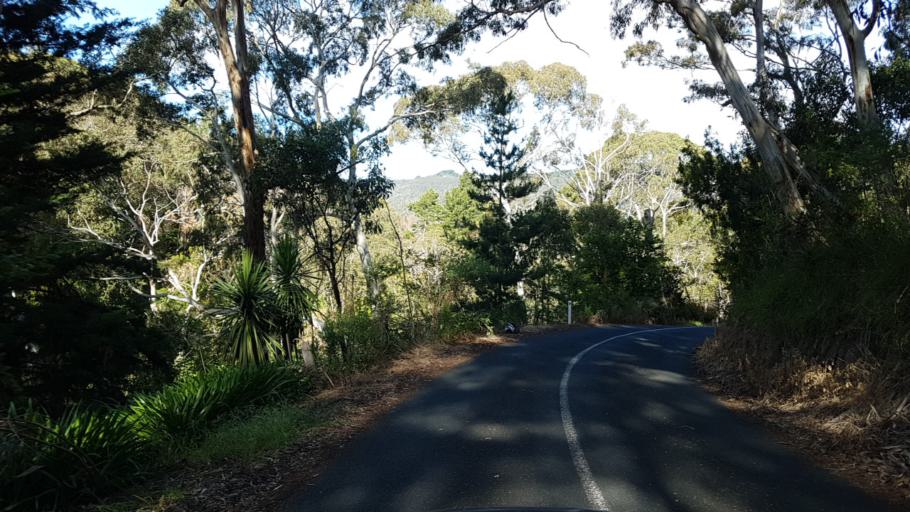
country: AU
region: South Australia
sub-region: Adelaide Hills
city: Adelaide Hills
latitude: -34.9098
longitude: 138.7669
